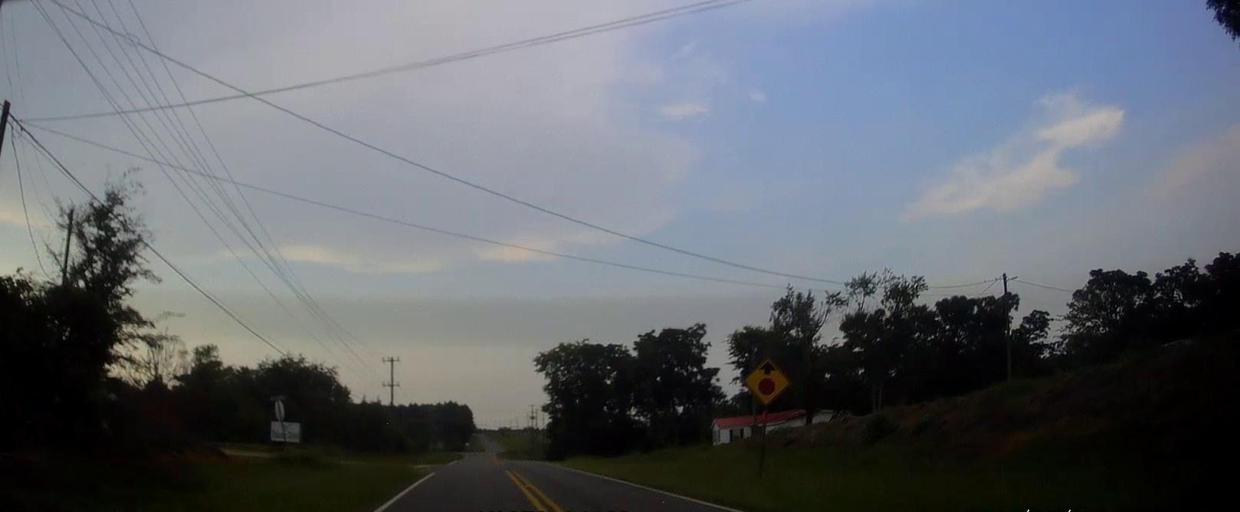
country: US
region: Georgia
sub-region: Laurens County
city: East Dublin
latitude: 32.5524
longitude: -82.8377
